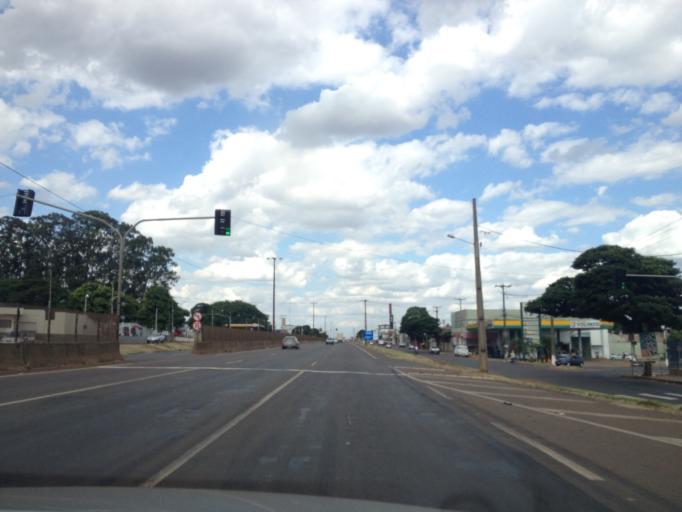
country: BR
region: Parana
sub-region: Sarandi
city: Sarandi
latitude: -23.4351
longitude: -51.8820
